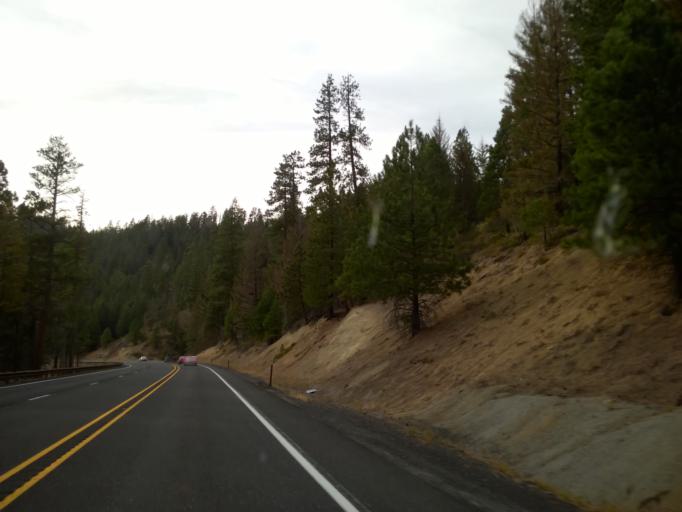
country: US
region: Washington
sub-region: Chelan County
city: Cashmere
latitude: 47.3360
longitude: -120.5881
